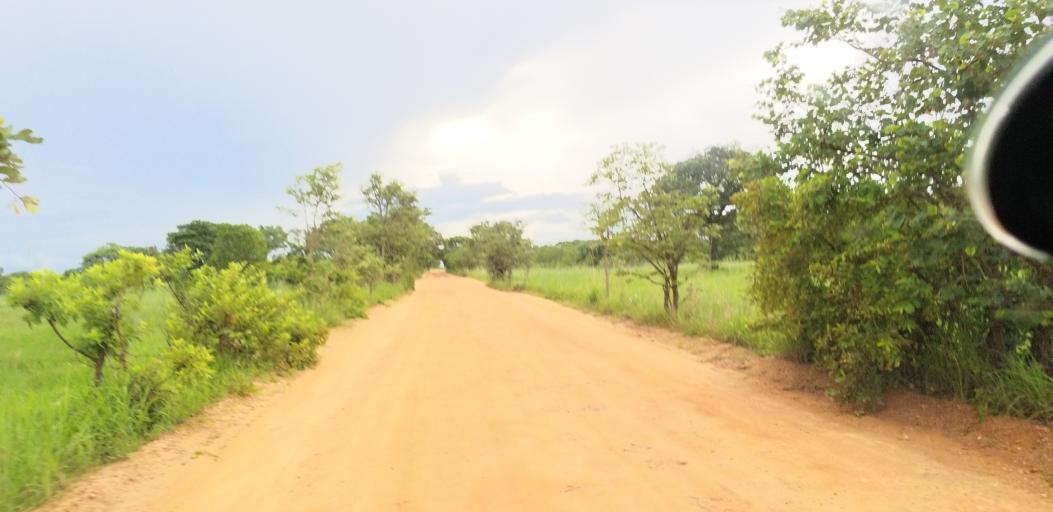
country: ZM
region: Lusaka
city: Chongwe
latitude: -15.1605
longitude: 28.4755
